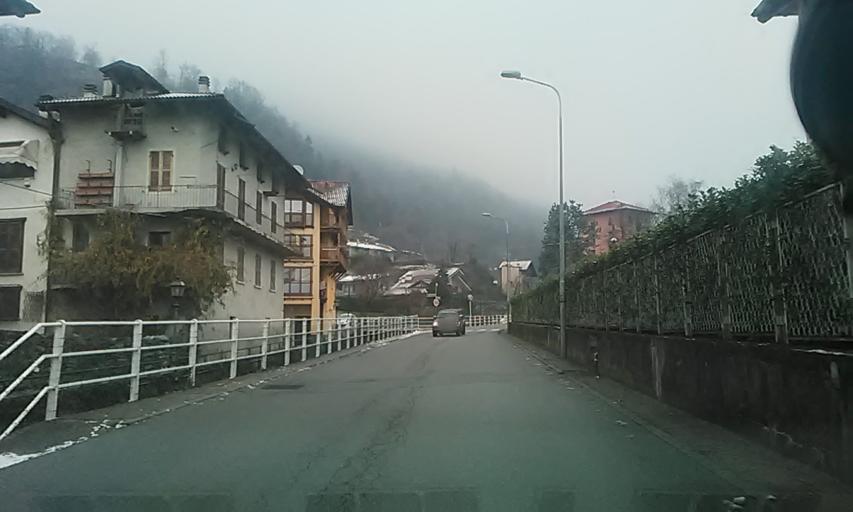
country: IT
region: Piedmont
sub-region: Provincia di Vercelli
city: Varallo
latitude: 45.8140
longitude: 8.2659
